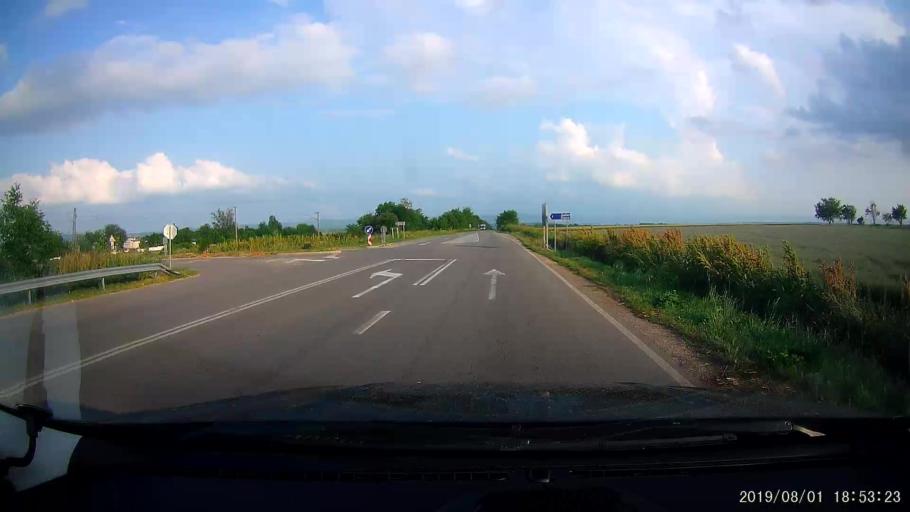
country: BG
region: Shumen
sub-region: Obshtina Shumen
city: Shumen
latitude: 43.2219
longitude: 26.9929
